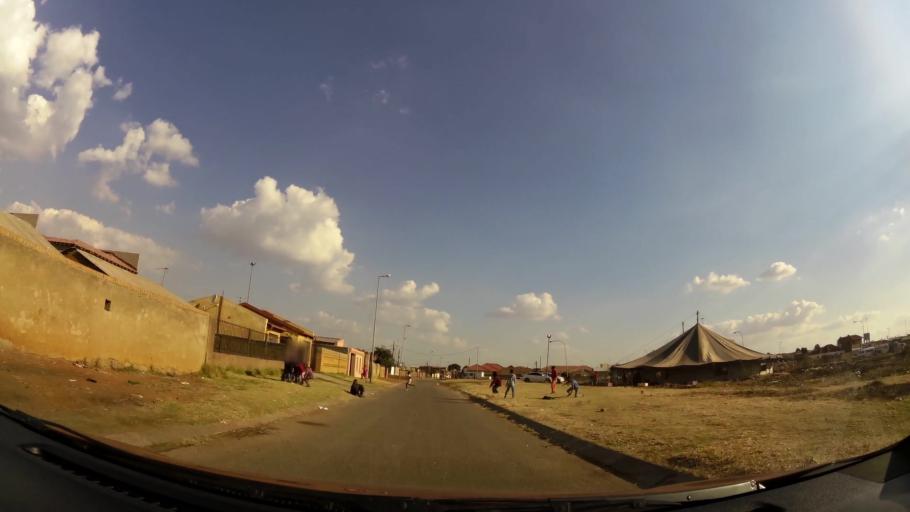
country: ZA
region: Gauteng
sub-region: City of Johannesburg Metropolitan Municipality
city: Soweto
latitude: -26.2312
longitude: 27.8663
